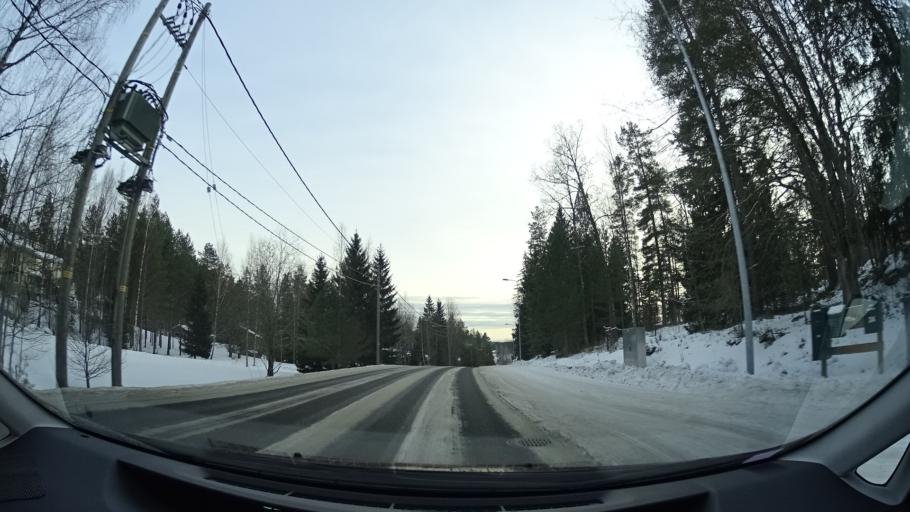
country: FI
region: Uusimaa
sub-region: Helsinki
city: Espoo
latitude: 60.2534
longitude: 24.5953
